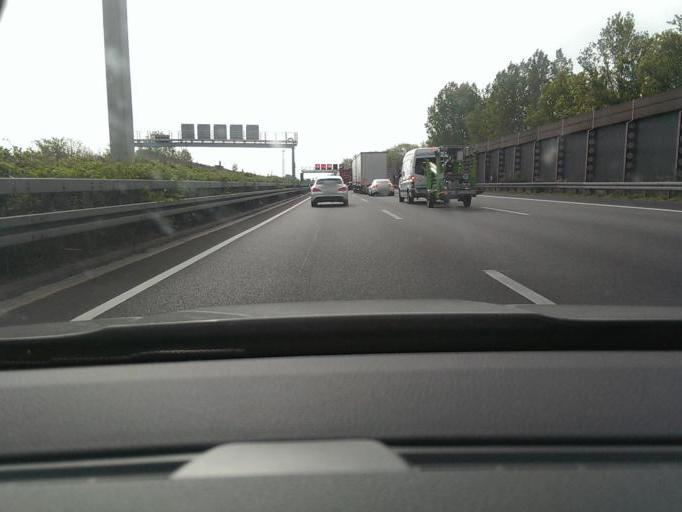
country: DE
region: Lower Saxony
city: Peine
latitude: 52.3405
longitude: 10.2227
